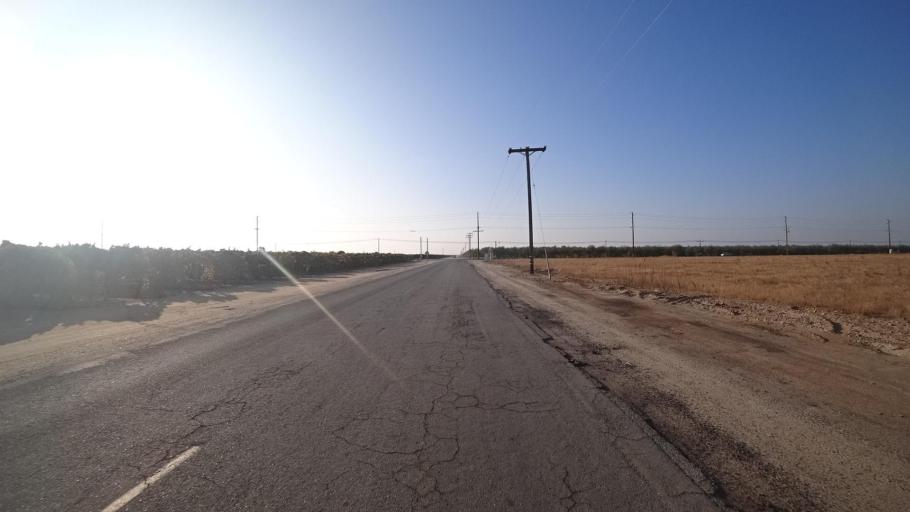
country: US
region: California
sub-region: Tulare County
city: Richgrove
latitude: 35.7774
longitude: -119.1340
